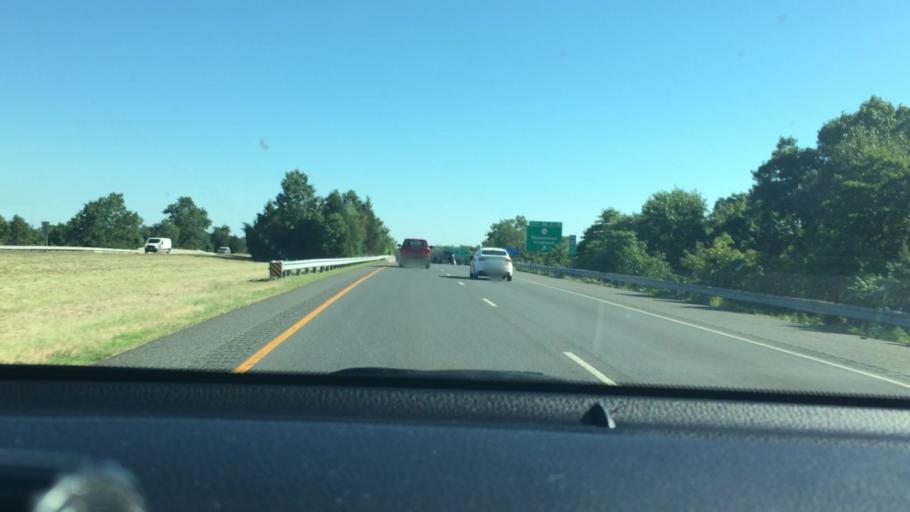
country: US
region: New Jersey
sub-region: Cumberland County
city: Vineland
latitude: 39.4934
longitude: -75.0706
